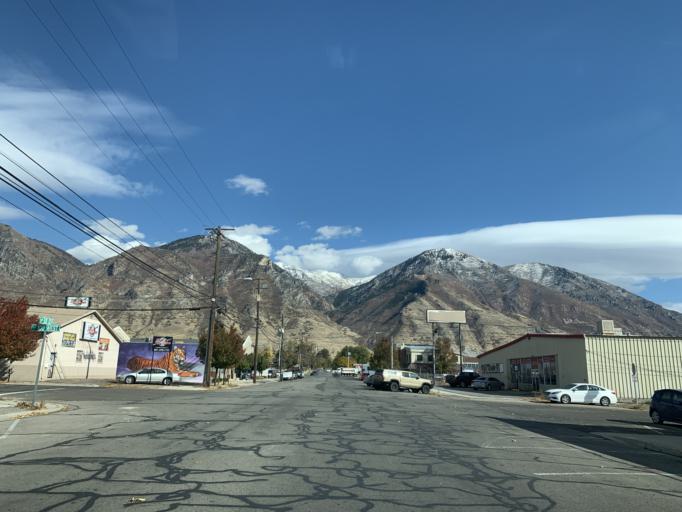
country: US
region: Utah
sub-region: Utah County
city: Provo
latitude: 40.2271
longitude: -111.6609
